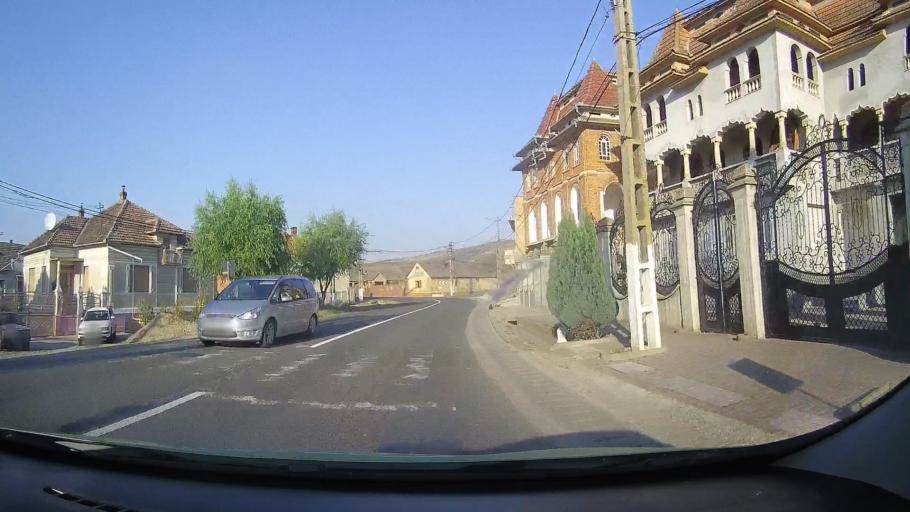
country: RO
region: Arad
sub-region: Comuna Covasint
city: Covasint
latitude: 46.2006
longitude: 21.6090
